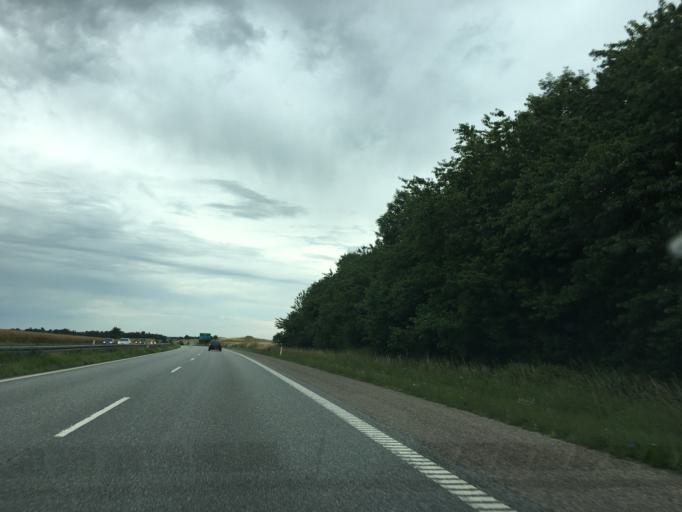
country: DK
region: Zealand
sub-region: Lejre Kommune
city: Norre Hvalso
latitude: 55.6430
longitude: 11.8465
